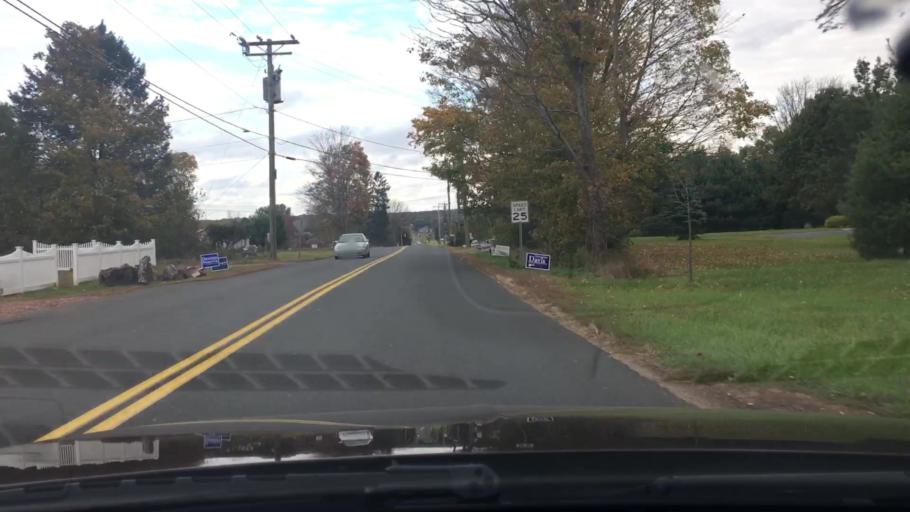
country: US
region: Connecticut
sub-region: Tolland County
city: Ellington
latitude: 41.9034
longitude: -72.4777
